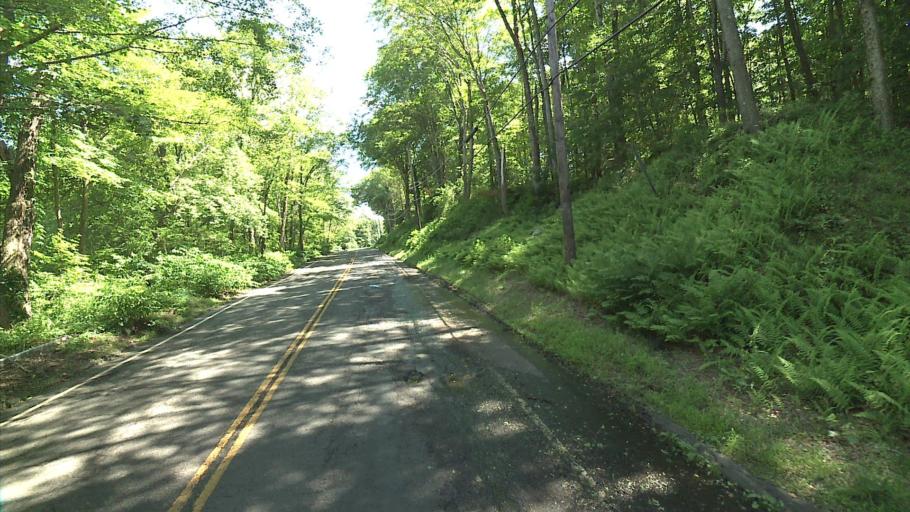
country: US
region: Connecticut
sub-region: New Haven County
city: Prospect
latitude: 41.4520
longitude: -72.9888
